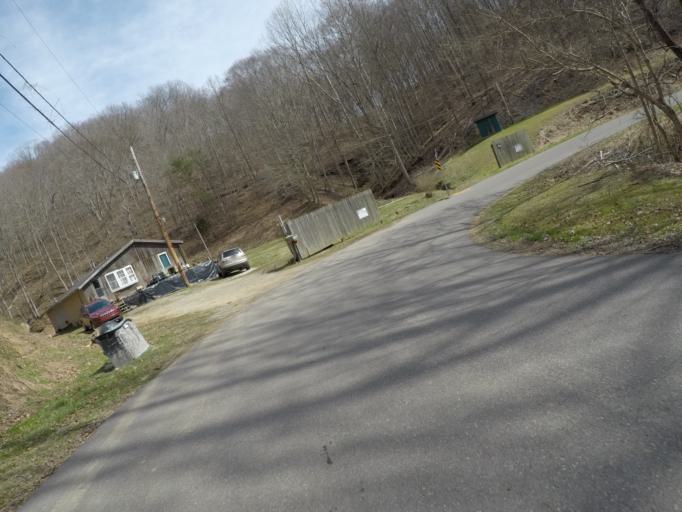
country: US
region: West Virginia
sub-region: Wayne County
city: Ceredo
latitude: 38.3758
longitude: -82.5518
